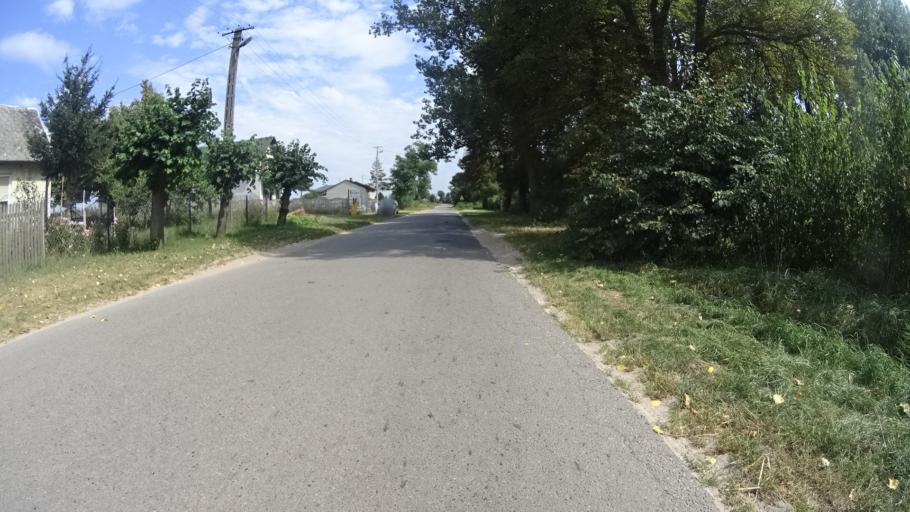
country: PL
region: Masovian Voivodeship
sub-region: Powiat bialobrzeski
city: Wysmierzyce
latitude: 51.6513
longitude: 20.7894
